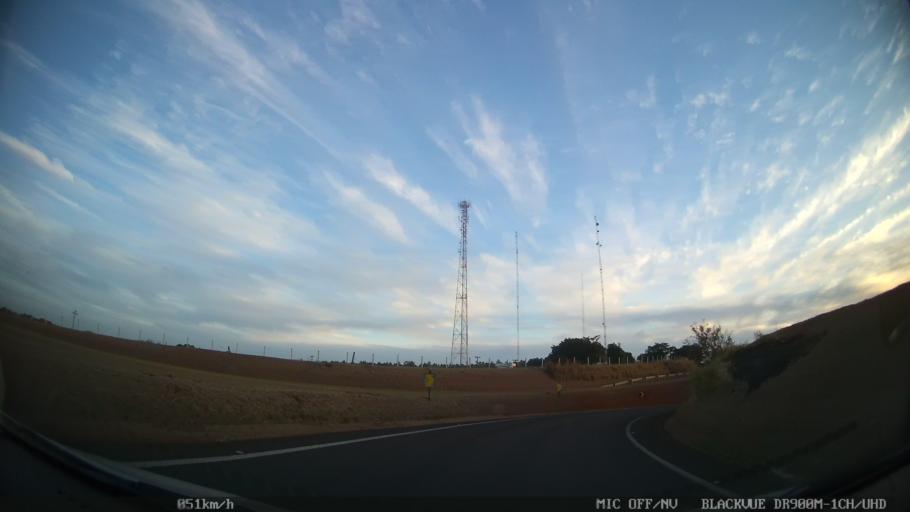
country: BR
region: Sao Paulo
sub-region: Pindorama
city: Pindorama
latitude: -21.2095
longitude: -48.9324
